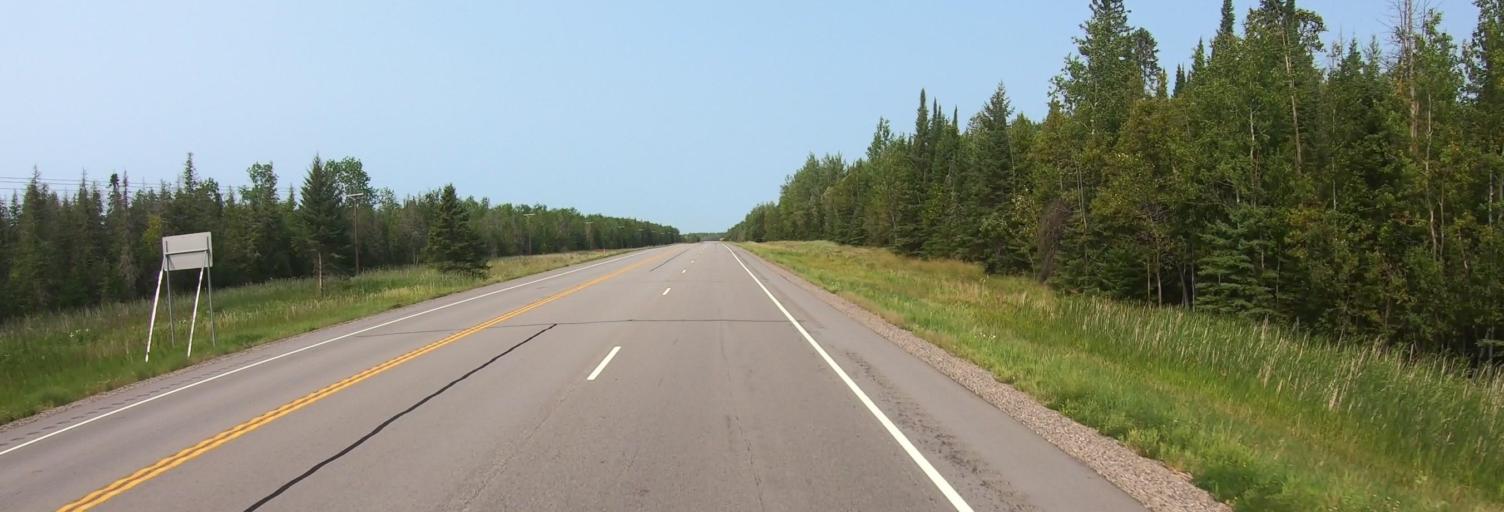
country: CA
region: Ontario
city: Fort Frances
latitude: 48.4034
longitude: -93.0278
